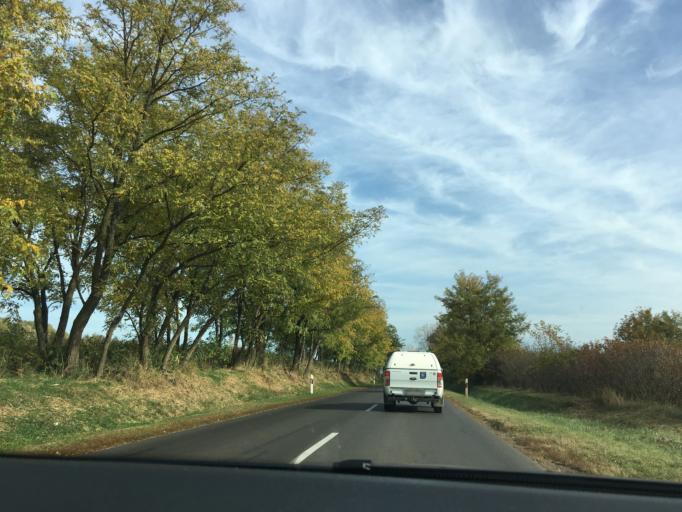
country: HU
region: Szabolcs-Szatmar-Bereg
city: Kisleta
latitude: 47.8548
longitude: 21.9907
